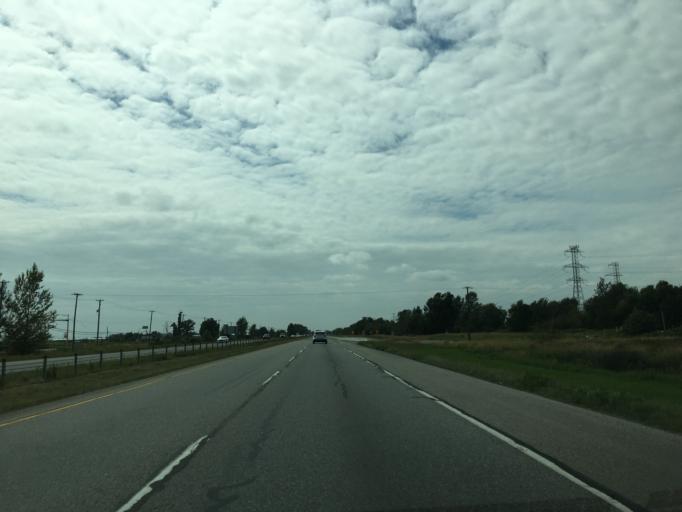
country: CA
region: British Columbia
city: Delta
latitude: 49.0905
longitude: -122.9773
